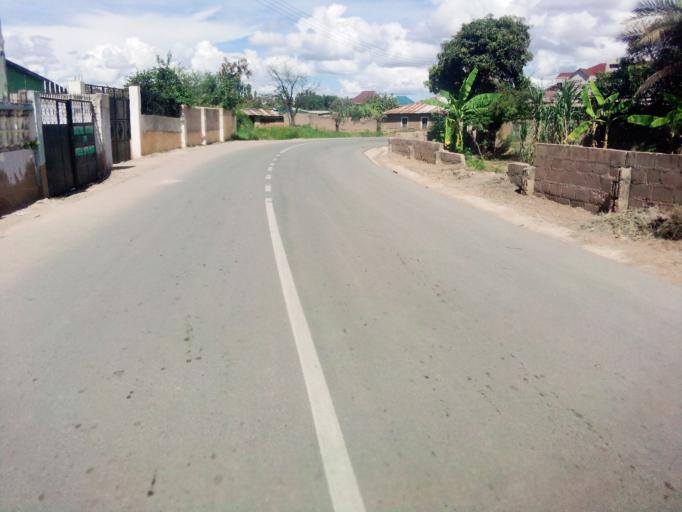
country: TZ
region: Dodoma
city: Dodoma
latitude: -6.1720
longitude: 35.7609
